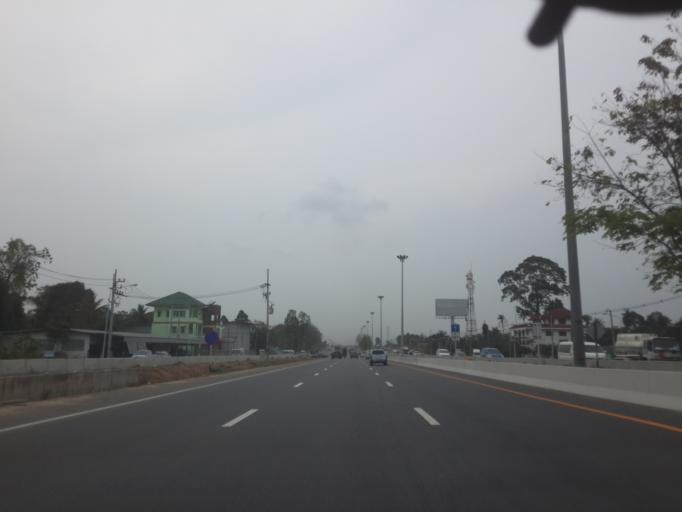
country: TH
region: Chon Buri
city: Ban Talat Bueng
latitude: 13.0524
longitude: 100.9961
